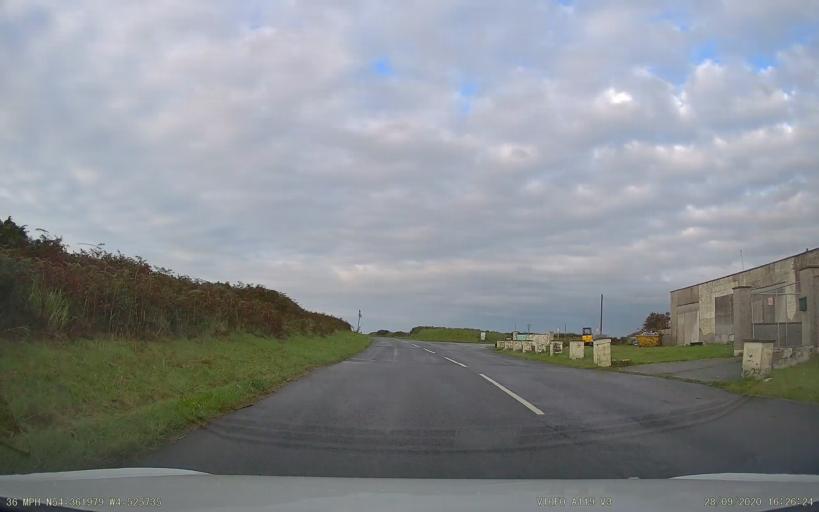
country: IM
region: Ramsey
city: Ramsey
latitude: 54.3620
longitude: -4.5257
